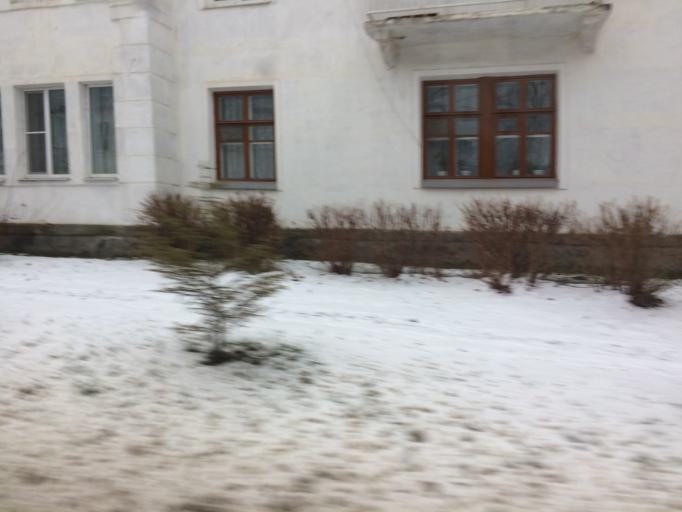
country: RU
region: Tula
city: Suvorov
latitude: 54.1188
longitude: 36.4949
